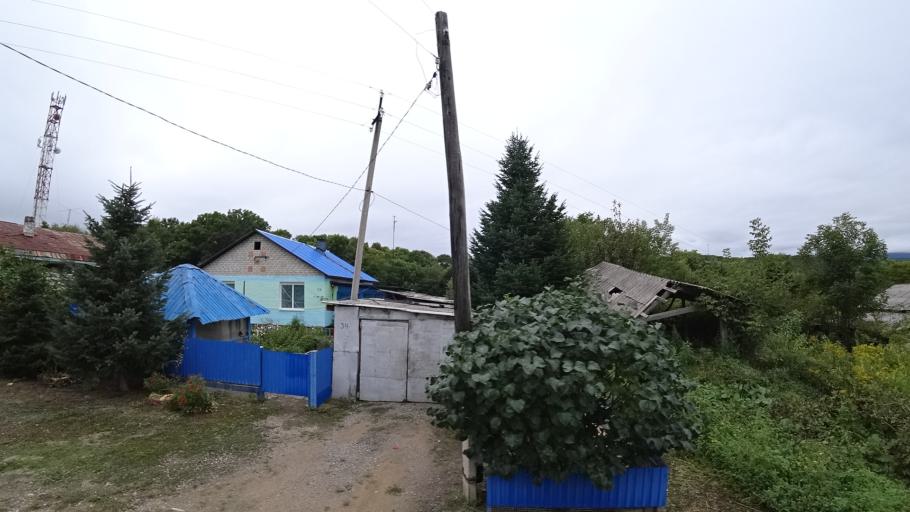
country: RU
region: Primorskiy
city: Rettikhovka
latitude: 44.1633
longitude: 132.7492
